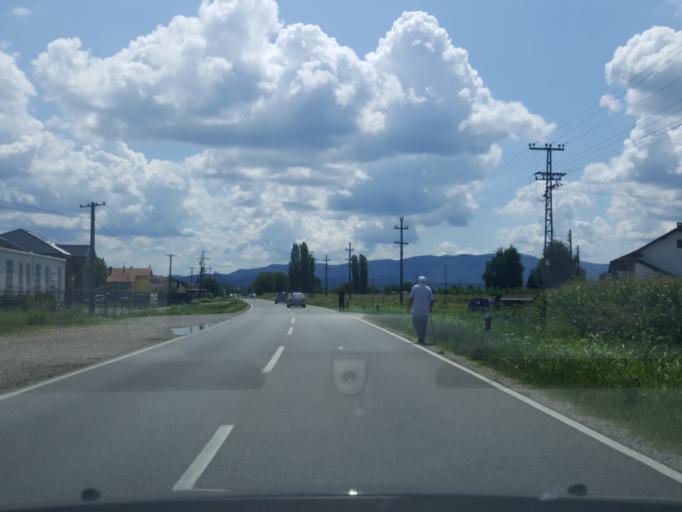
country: RS
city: Lipnicki Sor
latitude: 44.5696
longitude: 19.2404
